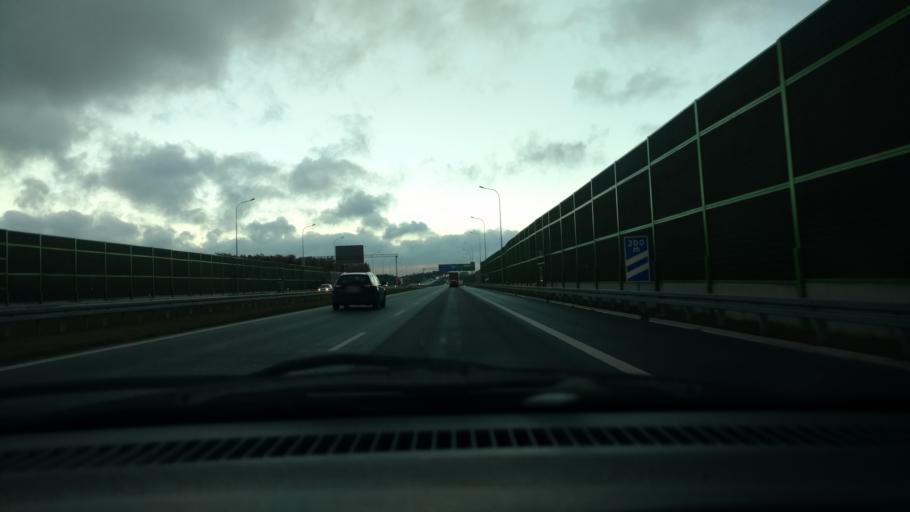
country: PL
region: Lodz Voivodeship
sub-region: Powiat lodzki wschodni
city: Andrespol
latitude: 51.7396
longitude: 19.6006
